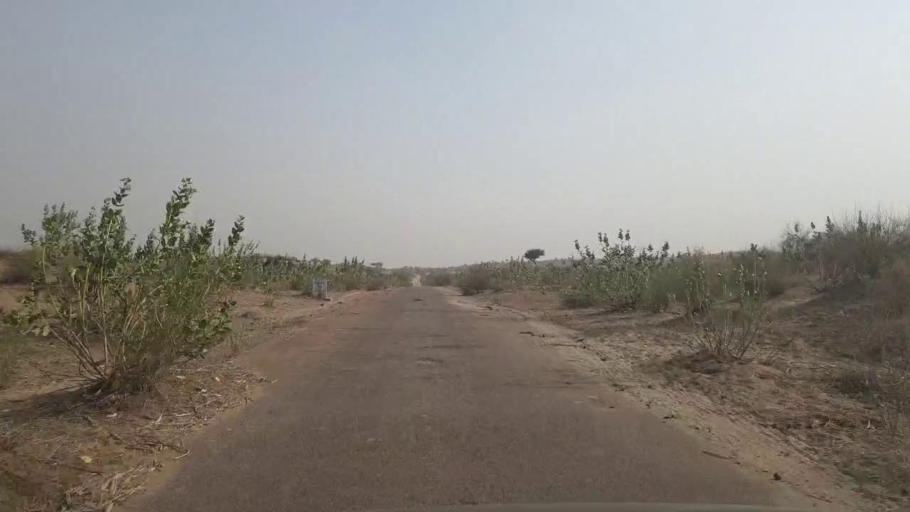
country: PK
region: Sindh
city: Chor
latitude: 25.5180
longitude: 69.9644
